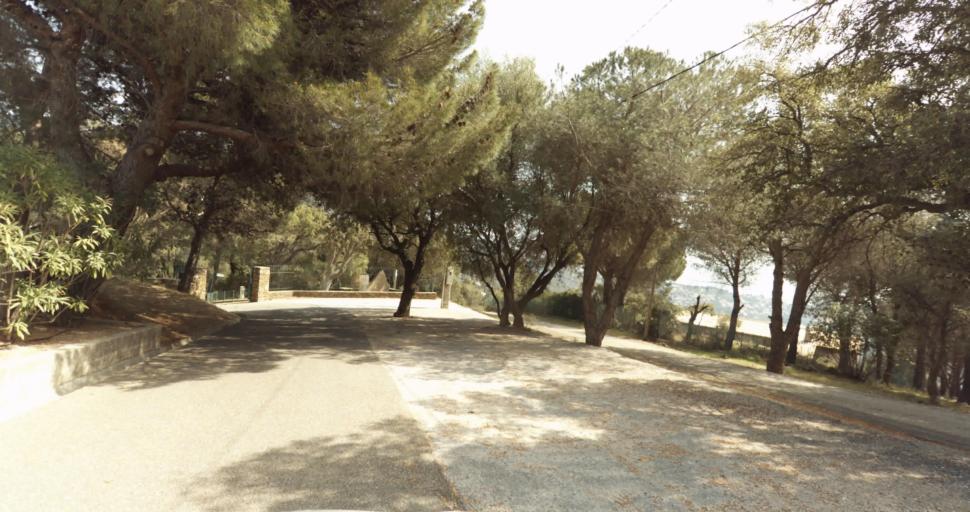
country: FR
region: Provence-Alpes-Cote d'Azur
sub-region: Departement du Var
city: Bormes-les-Mimosas
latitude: 43.1553
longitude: 6.3483
